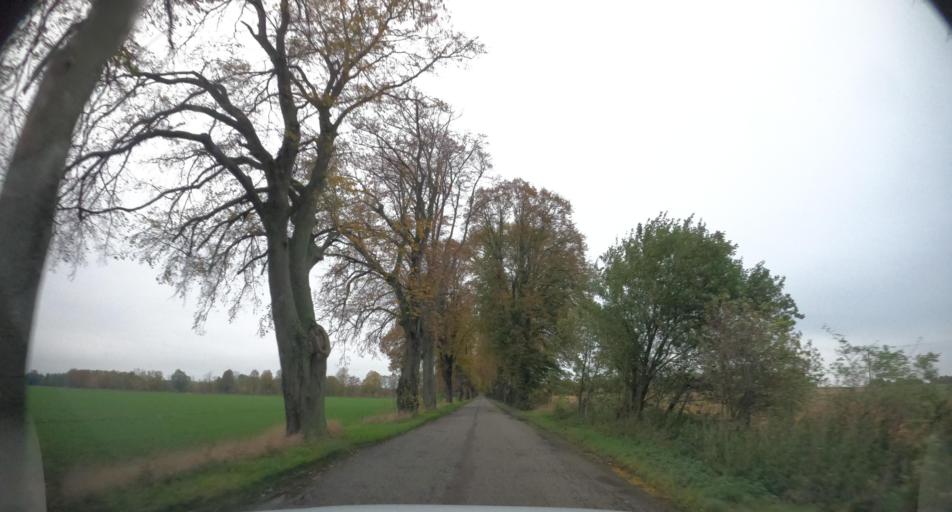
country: PL
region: West Pomeranian Voivodeship
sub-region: Powiat kamienski
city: Wolin
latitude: 53.9036
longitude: 14.6242
